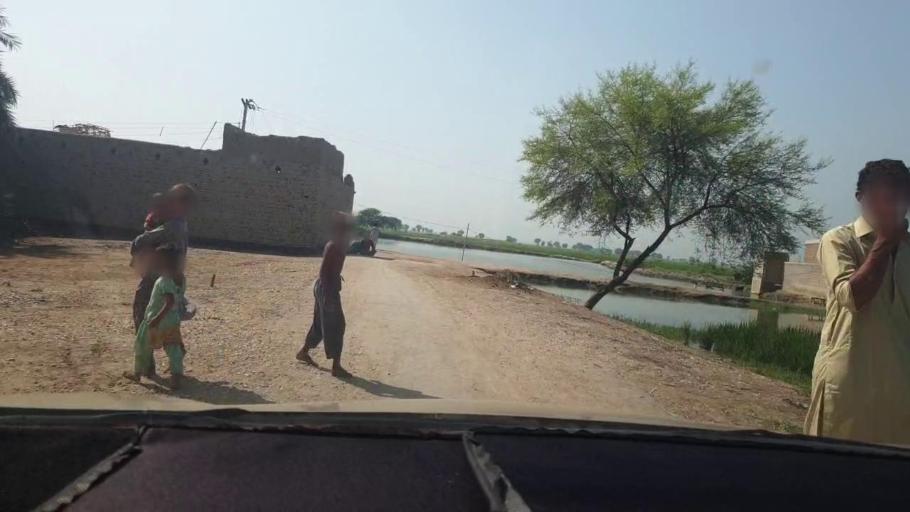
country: PK
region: Sindh
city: Kambar
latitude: 27.5587
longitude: 68.0594
